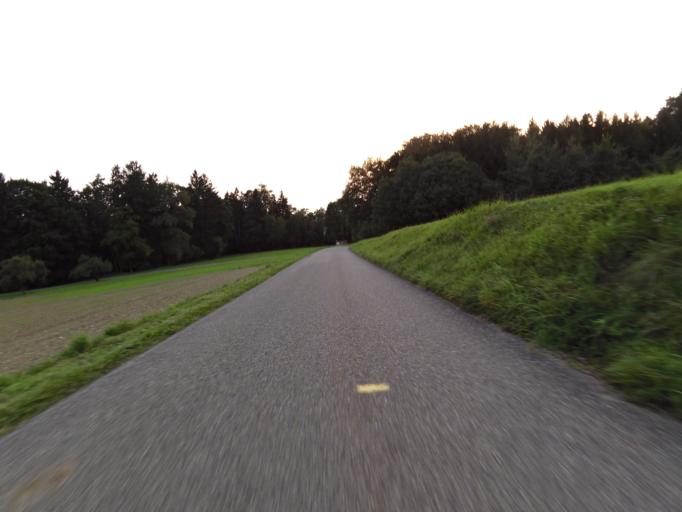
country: CH
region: Thurgau
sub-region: Frauenfeld District
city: Gachnang
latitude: 47.5371
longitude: 8.8696
